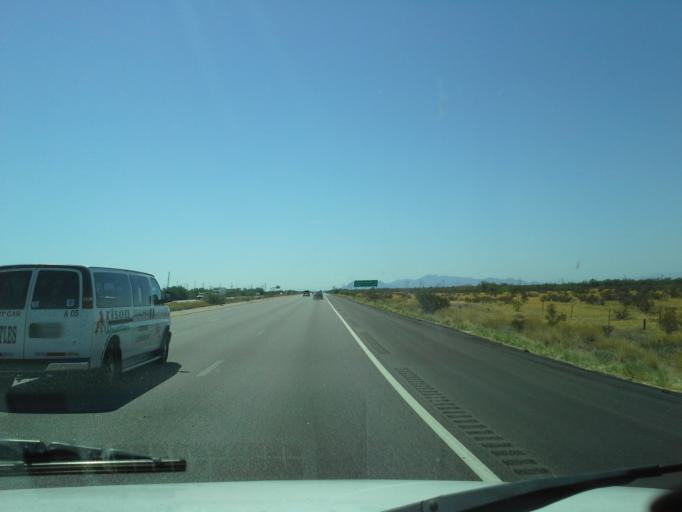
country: US
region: Arizona
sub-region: Pima County
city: Avra Valley
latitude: 32.5635
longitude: -111.3151
